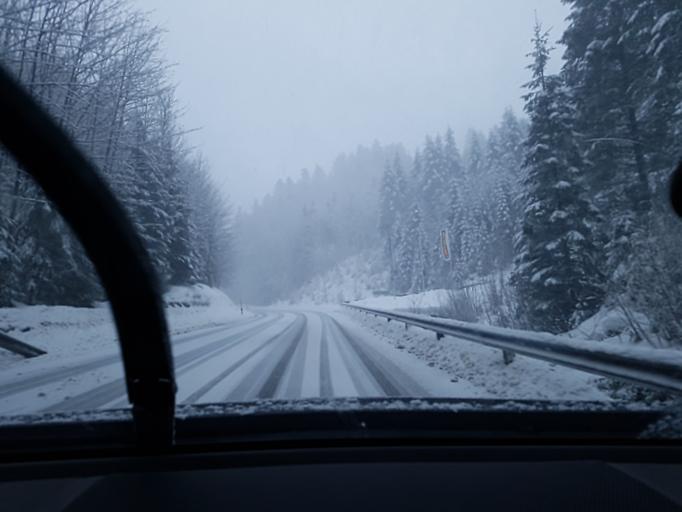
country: AT
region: Salzburg
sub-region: Politischer Bezirk Hallein
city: Abtenau
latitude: 47.5680
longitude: 13.3791
